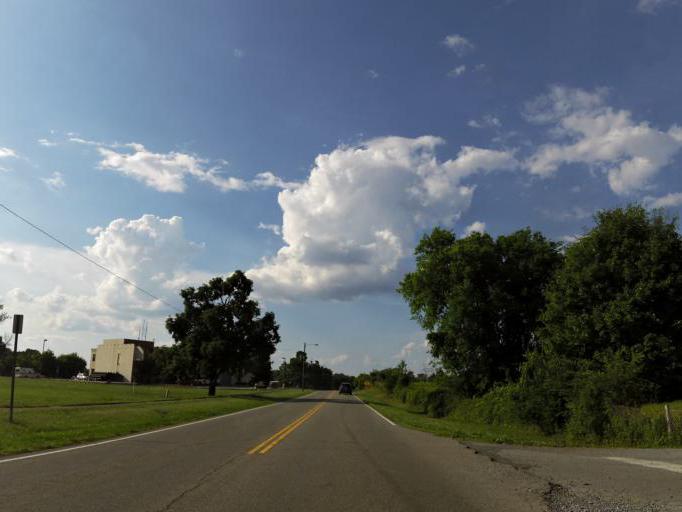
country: US
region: Tennessee
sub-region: Blount County
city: Alcoa
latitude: 35.7807
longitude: -83.9775
